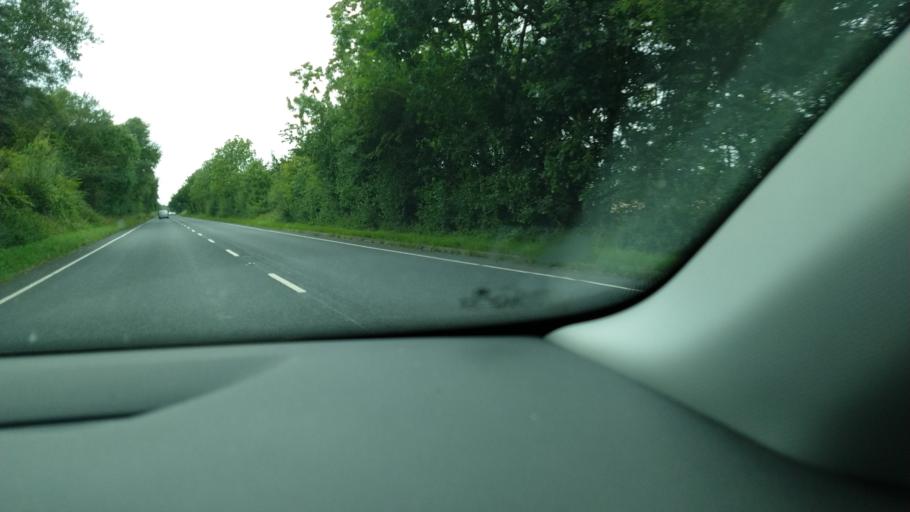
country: GB
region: England
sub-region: East Riding of Yorkshire
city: Barmby on the Marsh
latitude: 53.7191
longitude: -0.9714
